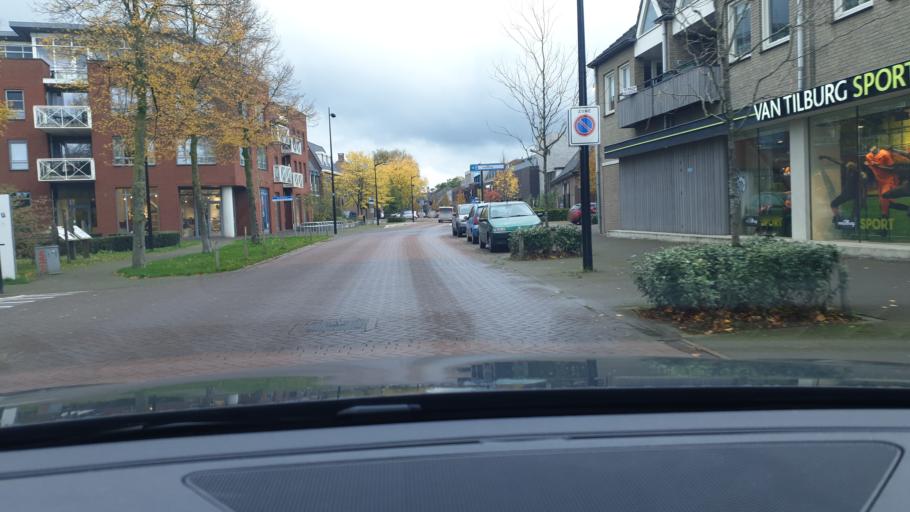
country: NL
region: North Brabant
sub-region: Gemeente Bernheze
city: Heesch
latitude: 51.7049
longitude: 5.5612
